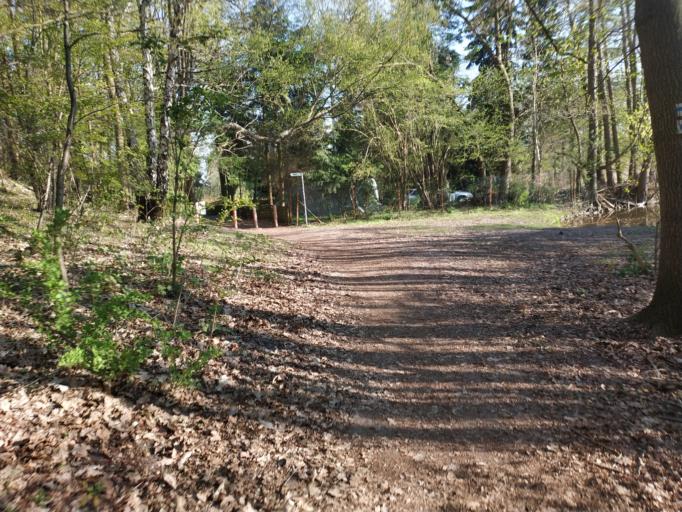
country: DE
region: Brandenburg
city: Strausberg
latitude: 52.5646
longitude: 13.8367
